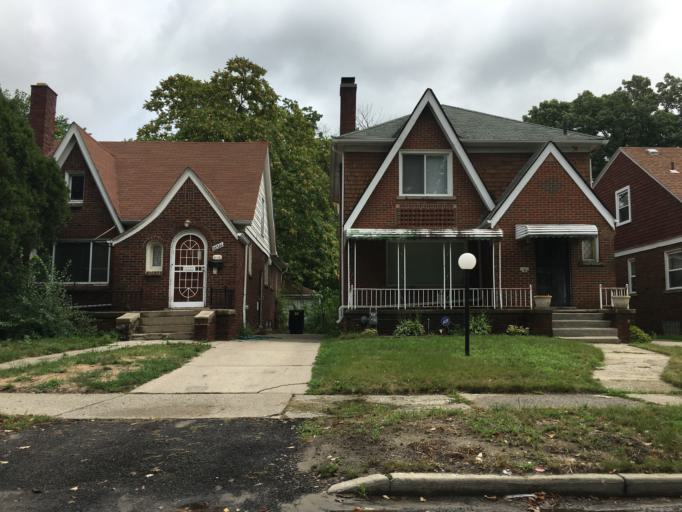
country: US
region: Michigan
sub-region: Oakland County
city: Ferndale
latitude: 42.4126
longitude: -83.1510
